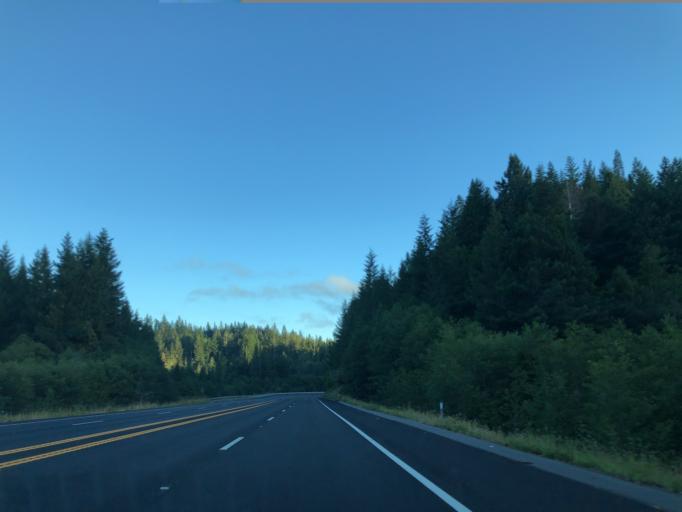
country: US
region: California
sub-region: Del Norte County
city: Bertsch-Oceanview
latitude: 41.4207
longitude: -123.9974
